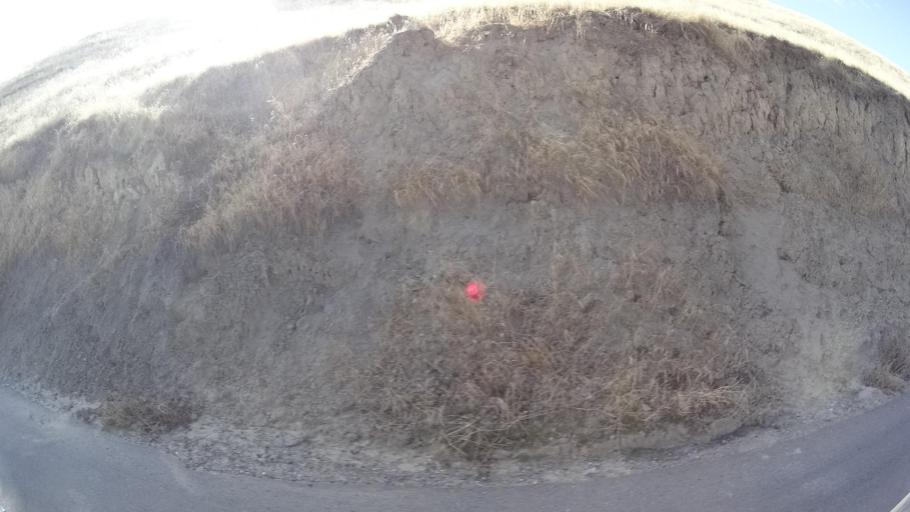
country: US
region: California
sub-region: Kern County
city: Oildale
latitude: 35.4956
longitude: -118.8925
